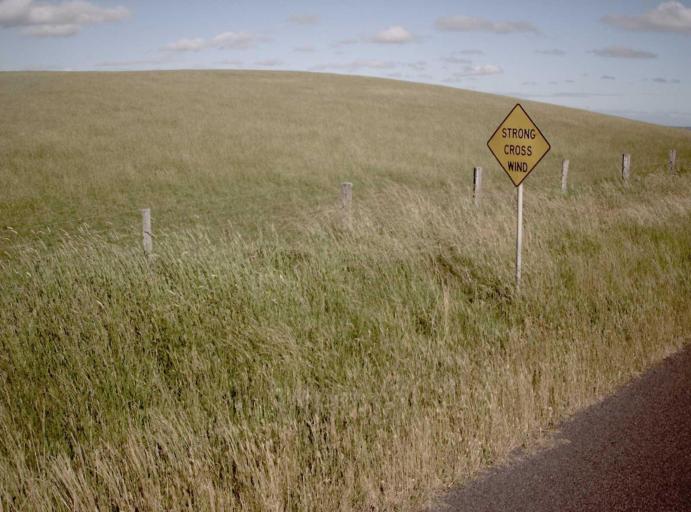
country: AU
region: Victoria
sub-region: Bass Coast
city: North Wonthaggi
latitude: -38.5355
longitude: 145.4549
